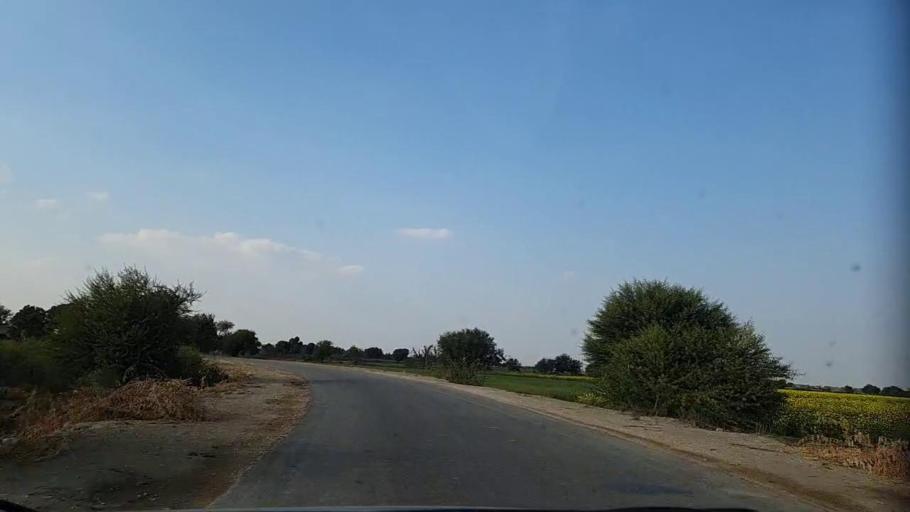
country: PK
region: Sindh
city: Pithoro
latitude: 25.6846
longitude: 69.2253
